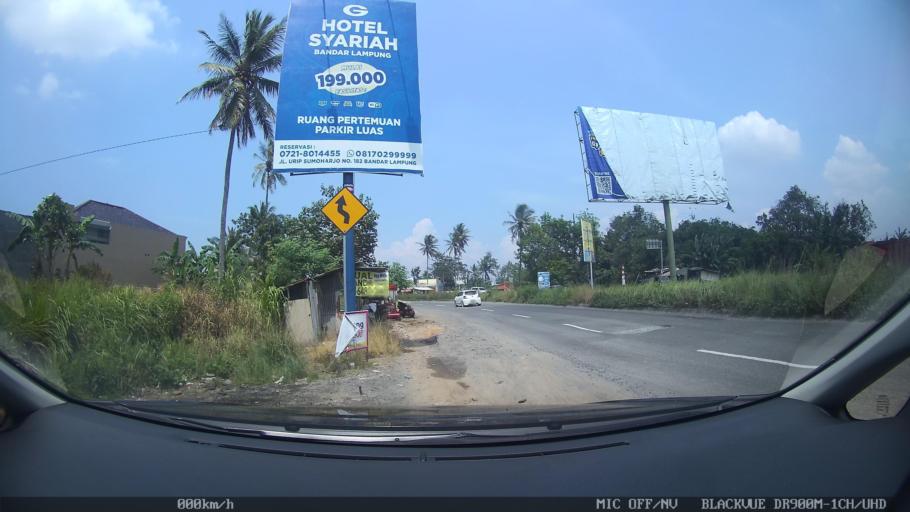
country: ID
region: Lampung
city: Kedaton
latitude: -5.3535
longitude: 105.3215
